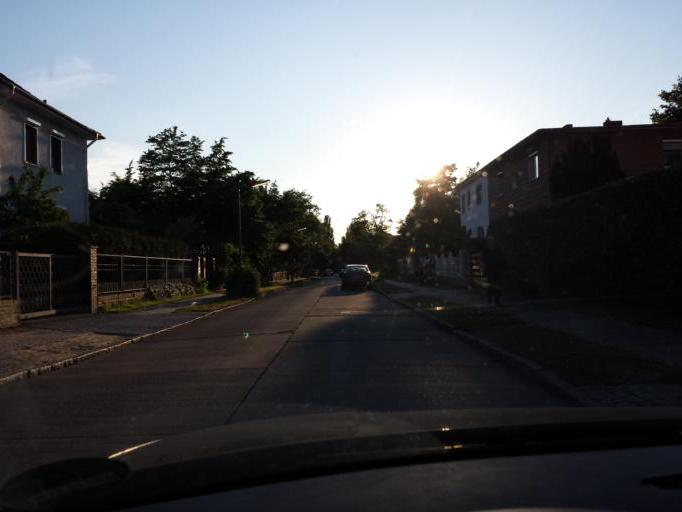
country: DE
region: Berlin
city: Mariendorf
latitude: 52.4232
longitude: 13.4011
